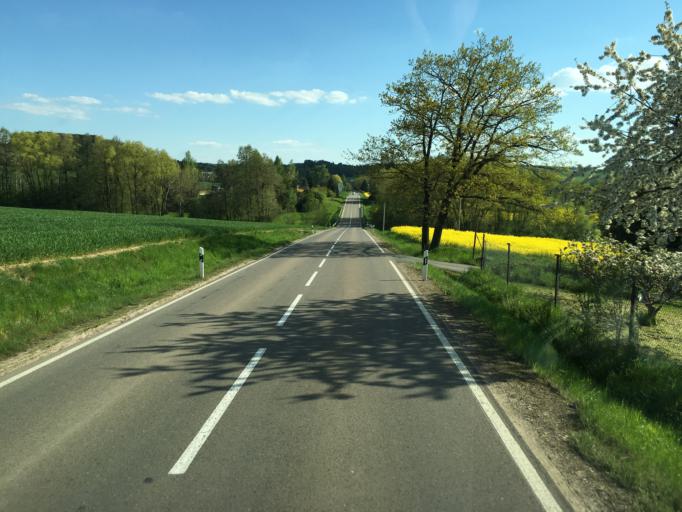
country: DE
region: Saxony
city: Rosswein
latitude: 51.0406
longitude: 13.1594
